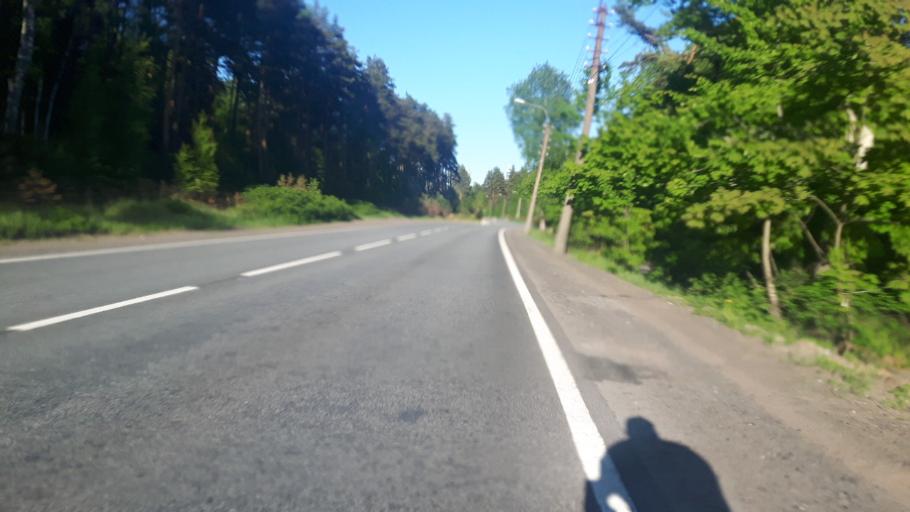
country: RU
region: Leningrad
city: Molodezhnoye
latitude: 60.1800
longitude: 29.4743
